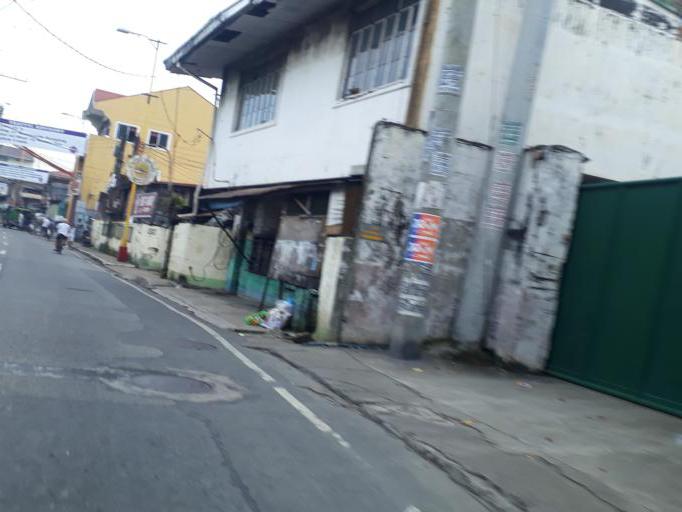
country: PH
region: Calabarzon
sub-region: Province of Rizal
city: Malabon
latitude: 14.6695
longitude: 120.9422
